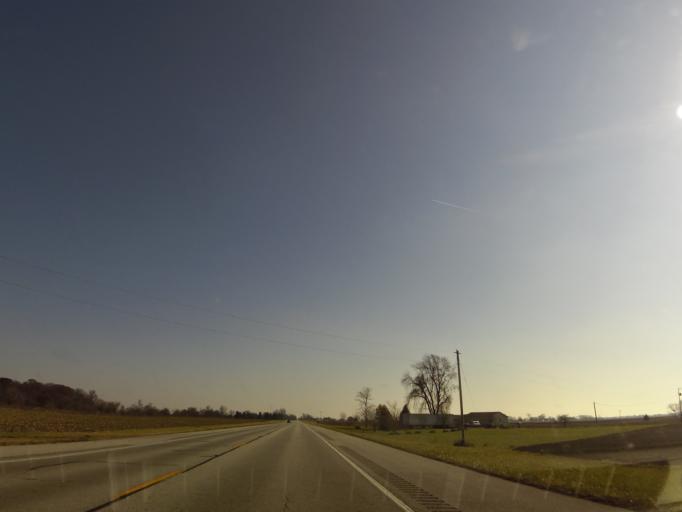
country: US
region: Indiana
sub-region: Union County
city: Liberty
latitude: 39.6074
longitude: -84.8812
